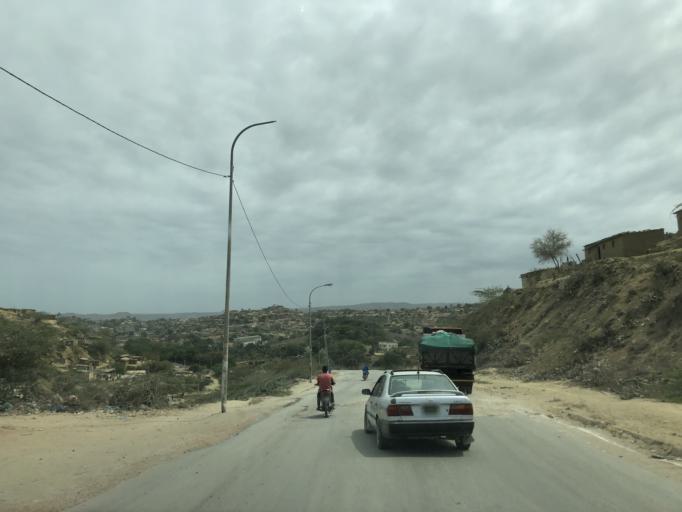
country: AO
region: Cuanza Sul
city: Sumbe
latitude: -11.2227
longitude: 13.8469
